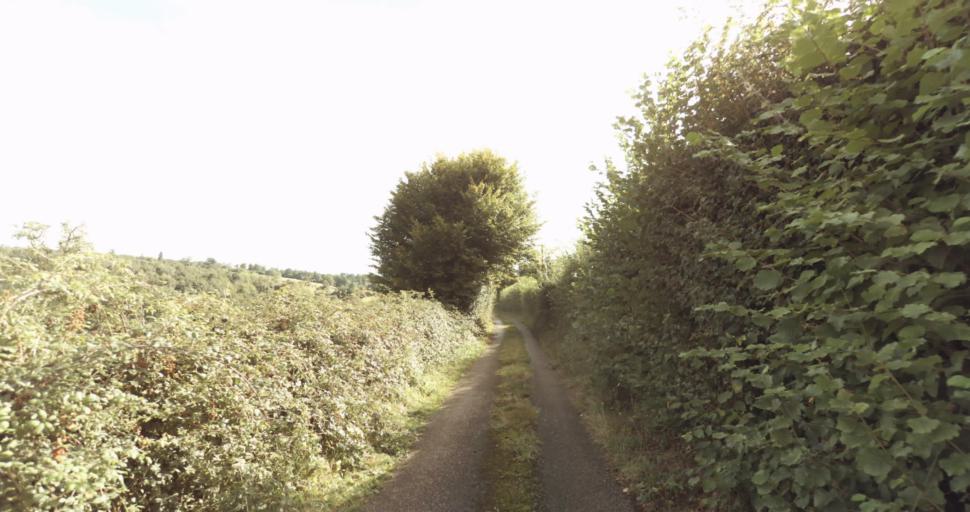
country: FR
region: Lower Normandy
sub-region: Departement de l'Orne
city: Vimoutiers
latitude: 48.8774
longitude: 0.1756
